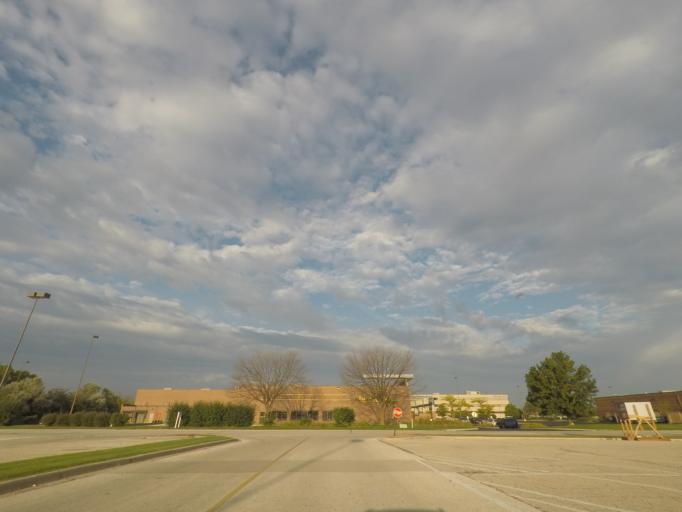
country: US
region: Wisconsin
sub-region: Waukesha County
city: Brookfield
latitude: 43.0348
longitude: -88.1111
